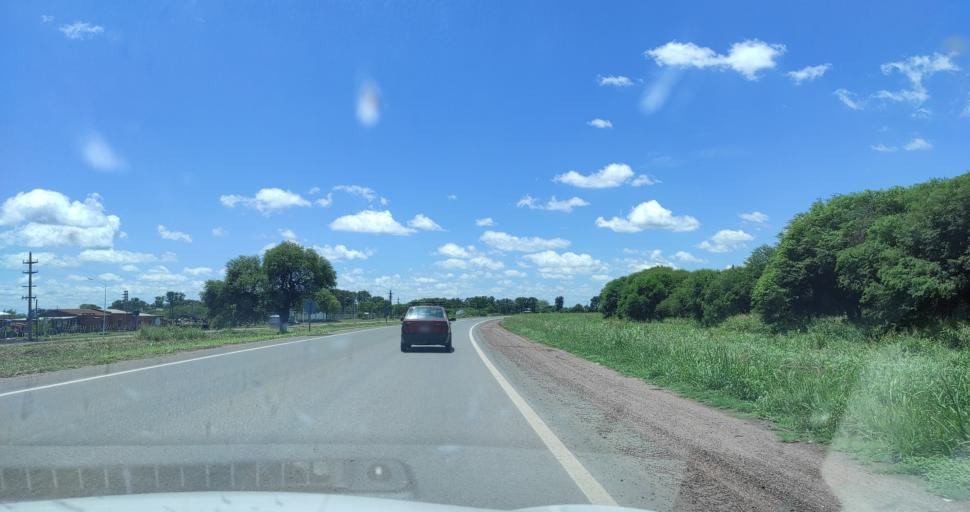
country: AR
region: Chaco
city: Avia Terai
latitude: -26.7039
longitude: -60.7433
